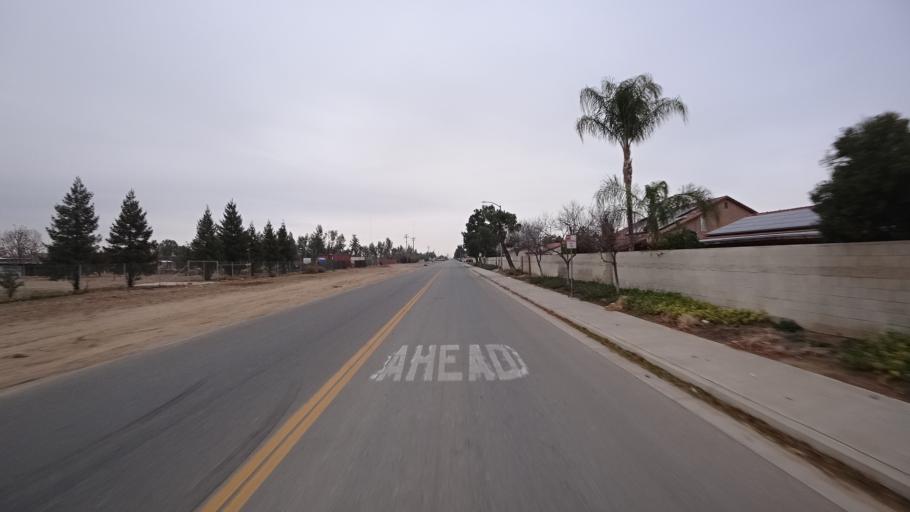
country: US
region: California
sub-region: Kern County
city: Bakersfield
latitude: 35.3485
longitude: -118.9410
